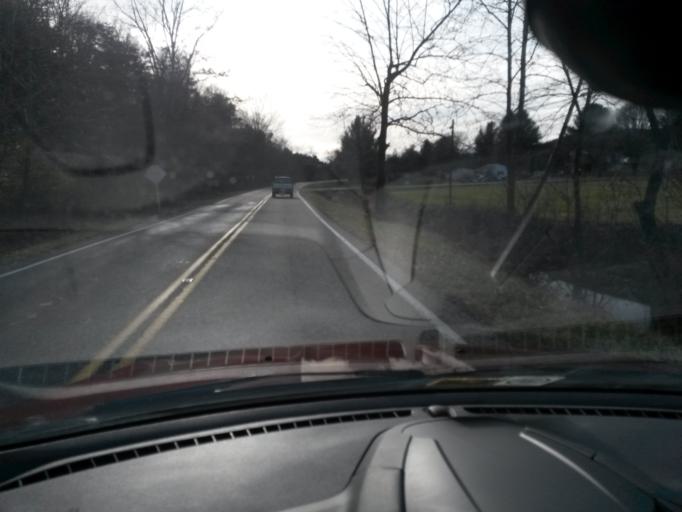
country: US
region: Virginia
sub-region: Rockbridge County
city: East Lexington
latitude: 38.0524
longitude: -79.4185
